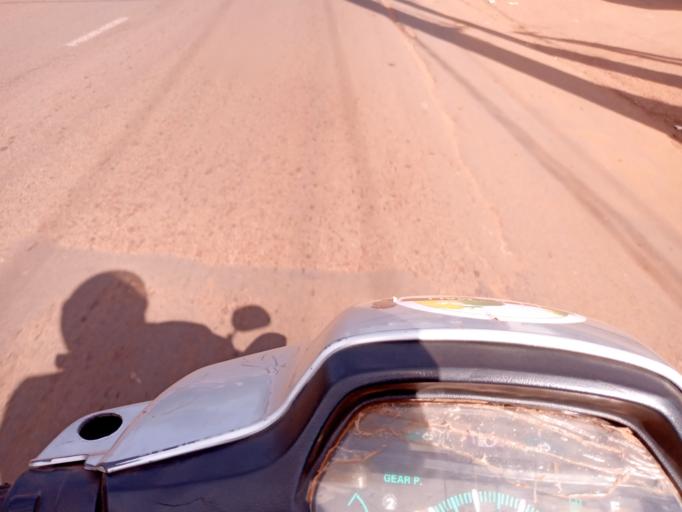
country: ML
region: Bamako
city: Bamako
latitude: 12.6649
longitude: -7.9375
